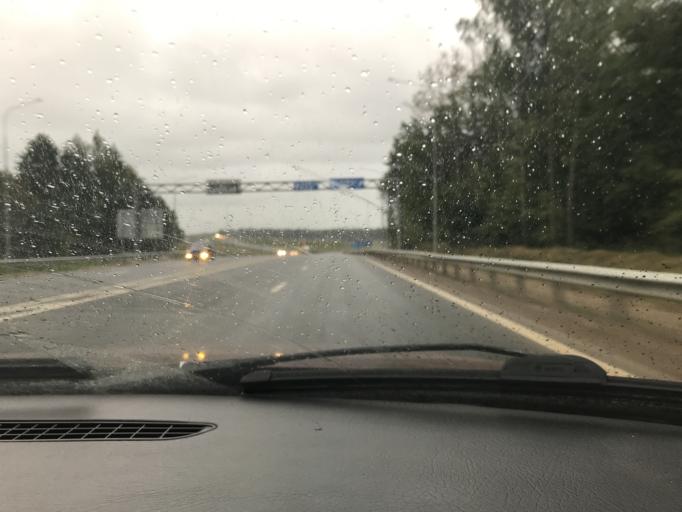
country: RU
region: Kaluga
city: Mstikhino
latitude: 54.5897
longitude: 36.0656
